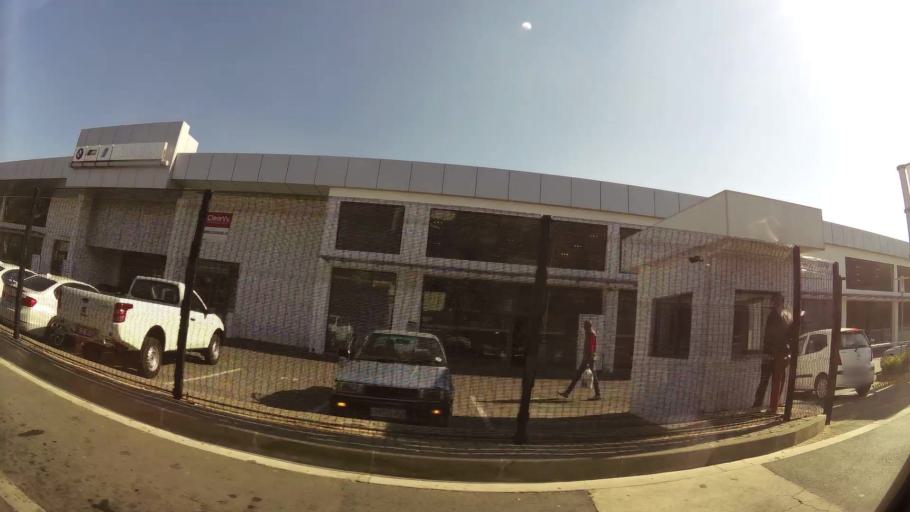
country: ZA
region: Gauteng
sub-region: City of Johannesburg Metropolitan Municipality
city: Johannesburg
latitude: -26.2635
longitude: 28.0588
